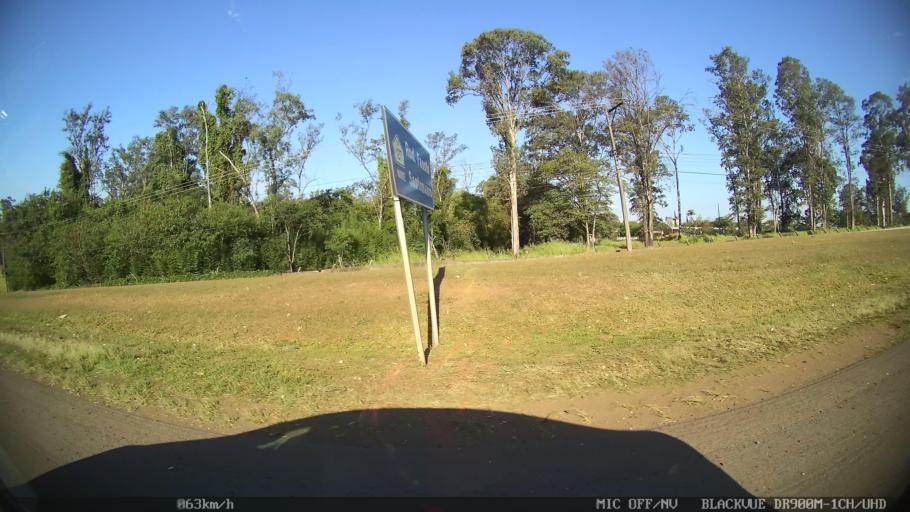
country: BR
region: Sao Paulo
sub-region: Piracicaba
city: Piracicaba
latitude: -22.6969
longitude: -47.6522
